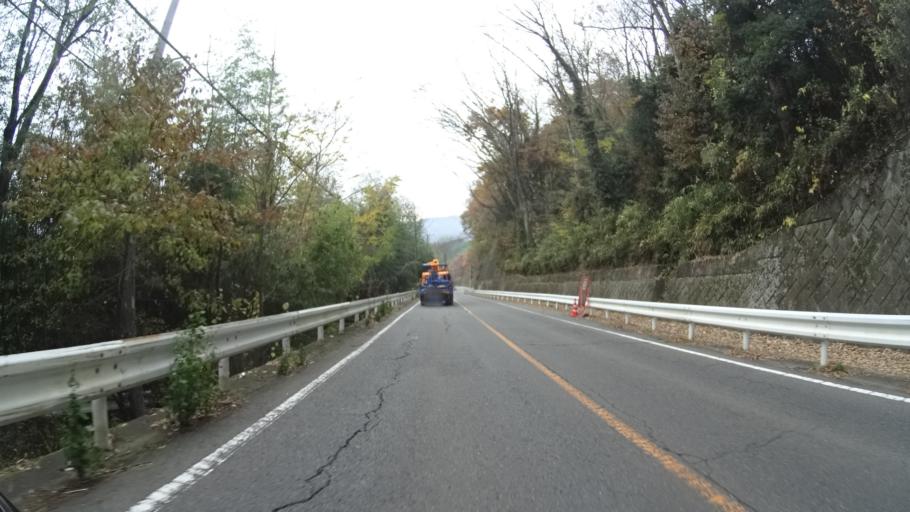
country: JP
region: Gunma
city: Numata
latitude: 36.6290
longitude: 139.0461
